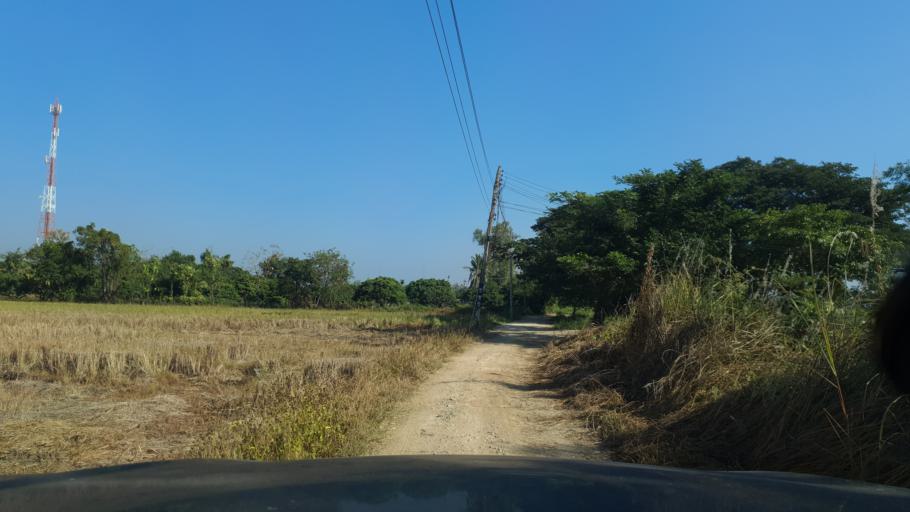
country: TH
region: Chiang Mai
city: Saraphi
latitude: 18.7179
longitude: 99.0748
